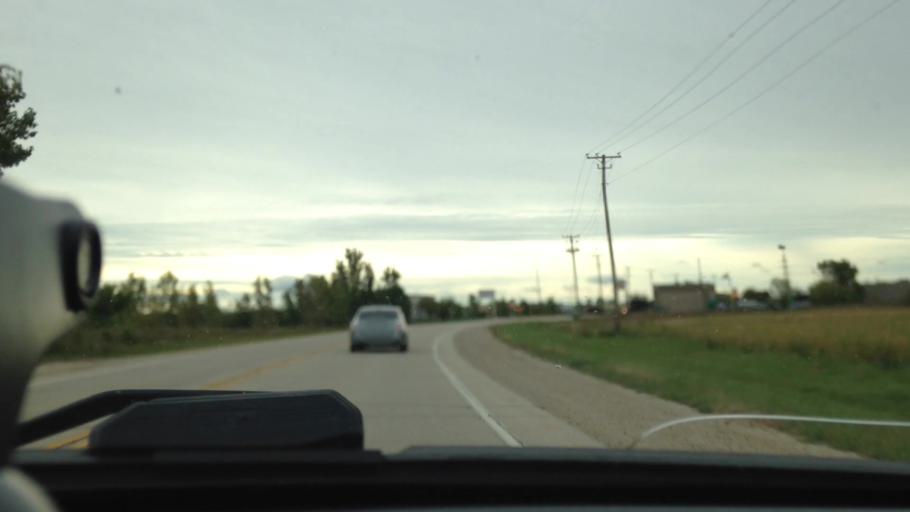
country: US
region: Wisconsin
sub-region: Fond du Lac County
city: North Fond du Lac
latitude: 43.7951
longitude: -88.4873
